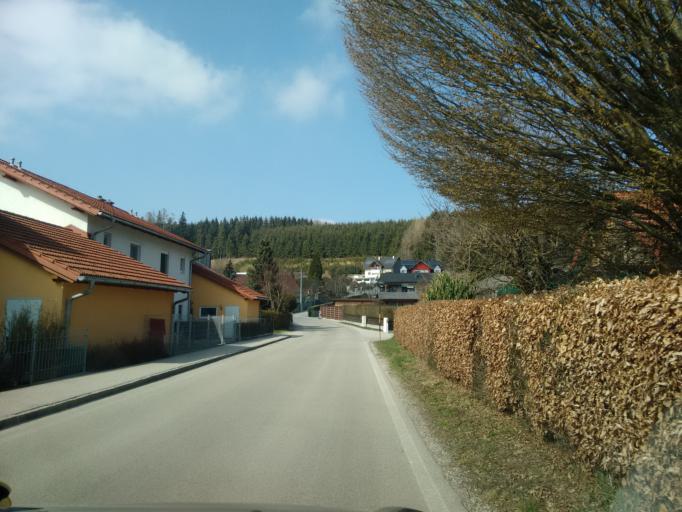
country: AT
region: Upper Austria
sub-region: Politischer Bezirk Grieskirchen
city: Bad Schallerbach
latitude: 48.1941
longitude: 13.9683
